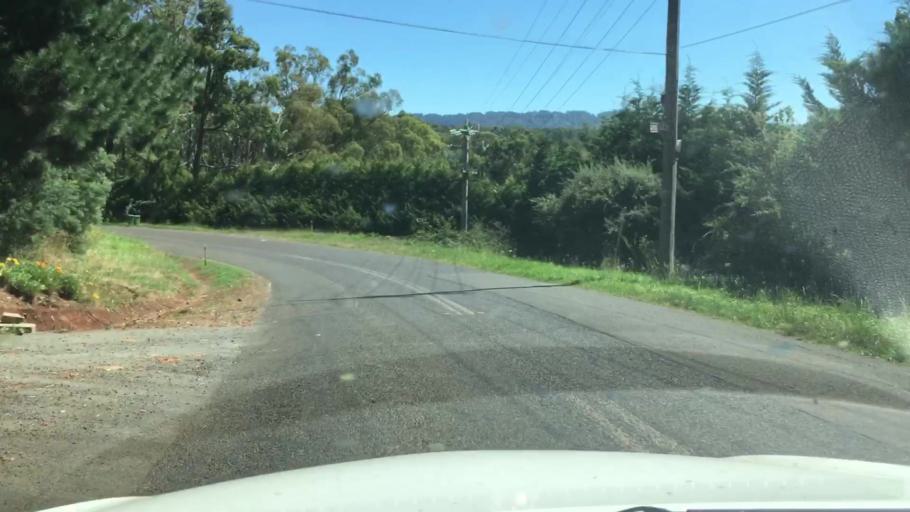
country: AU
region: Victoria
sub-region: Yarra Ranges
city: Mount Evelyn
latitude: -37.8158
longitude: 145.4222
